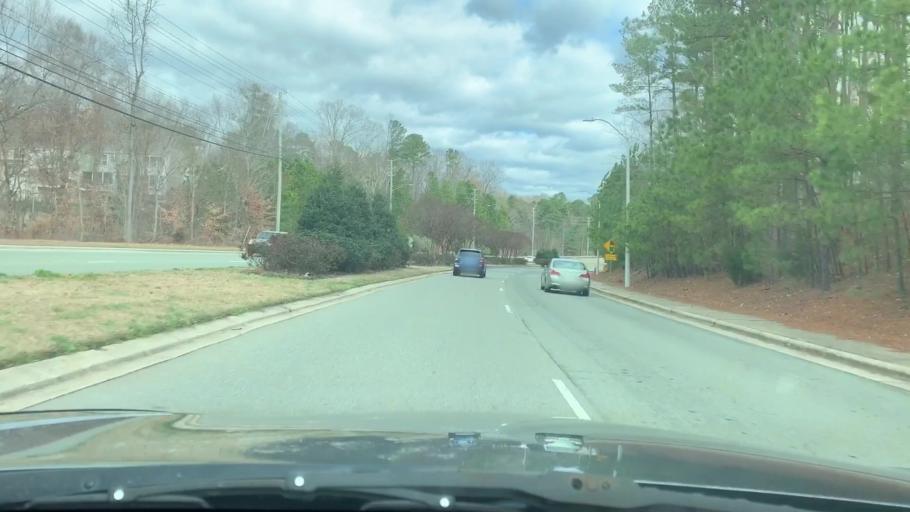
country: US
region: North Carolina
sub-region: Wake County
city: Cary
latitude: 35.8072
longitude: -78.7827
